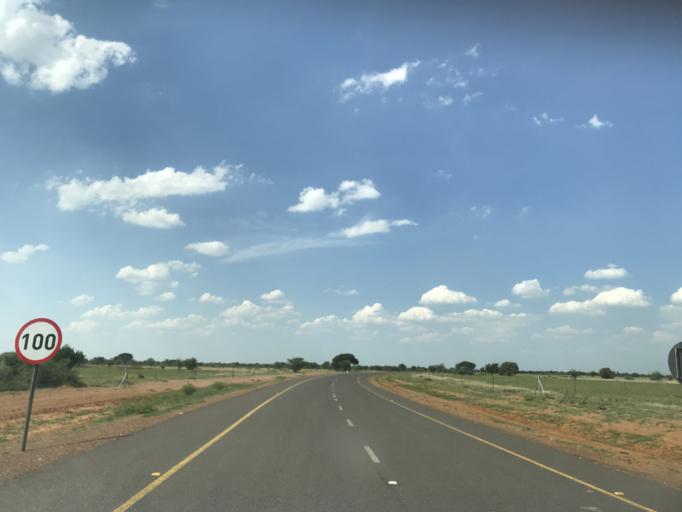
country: BW
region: South East
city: Janeng
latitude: -25.5549
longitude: 25.5983
